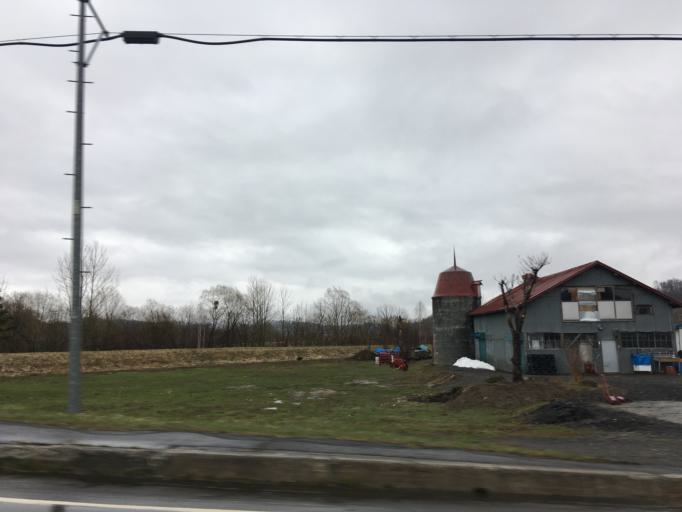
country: JP
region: Hokkaido
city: Nayoro
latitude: 44.1125
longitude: 142.4795
